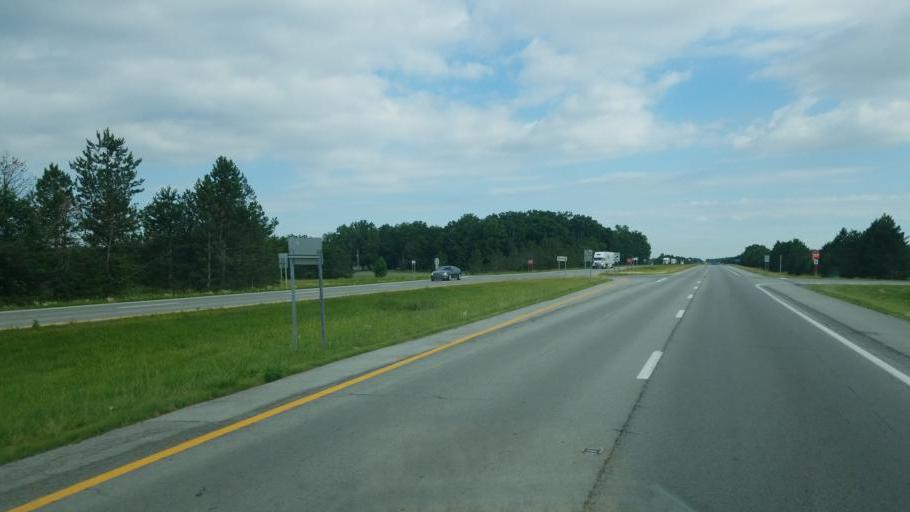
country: US
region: Ohio
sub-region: Wyandot County
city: Carey
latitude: 40.8900
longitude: -83.3387
